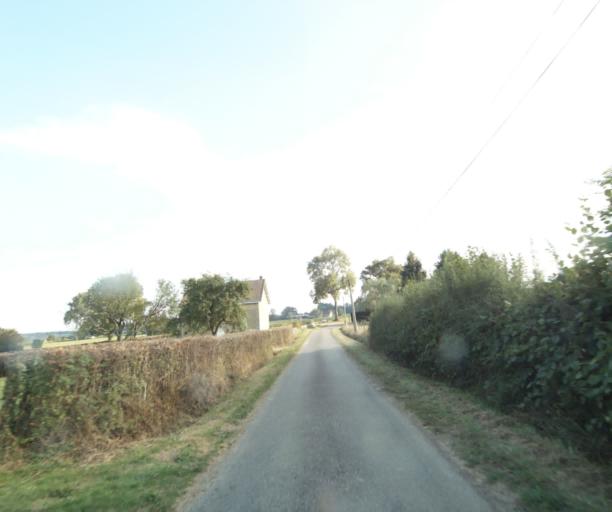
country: FR
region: Bourgogne
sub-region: Departement de Saone-et-Loire
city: Paray-le-Monial
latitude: 46.5243
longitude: 4.1222
